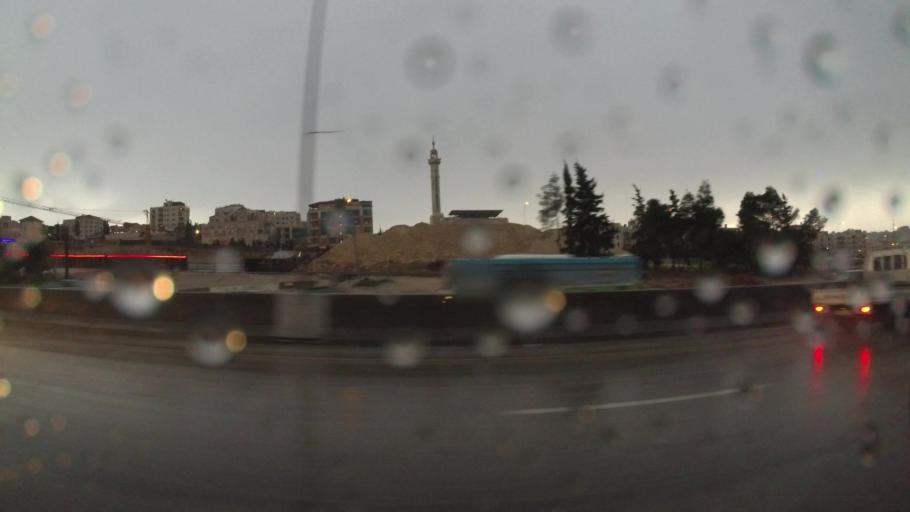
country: JO
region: Amman
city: Umm as Summaq
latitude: 31.9079
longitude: 35.8662
